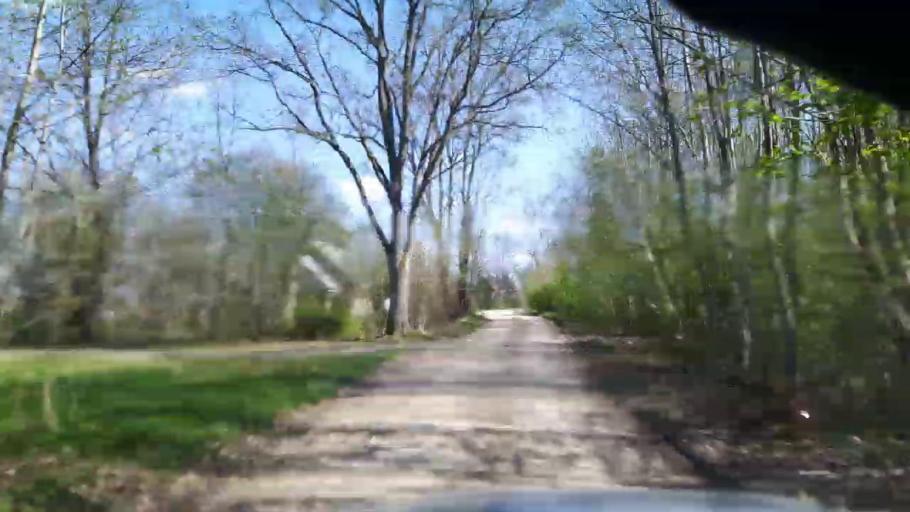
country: EE
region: Paernumaa
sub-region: Tootsi vald
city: Tootsi
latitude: 58.5379
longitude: 24.8285
